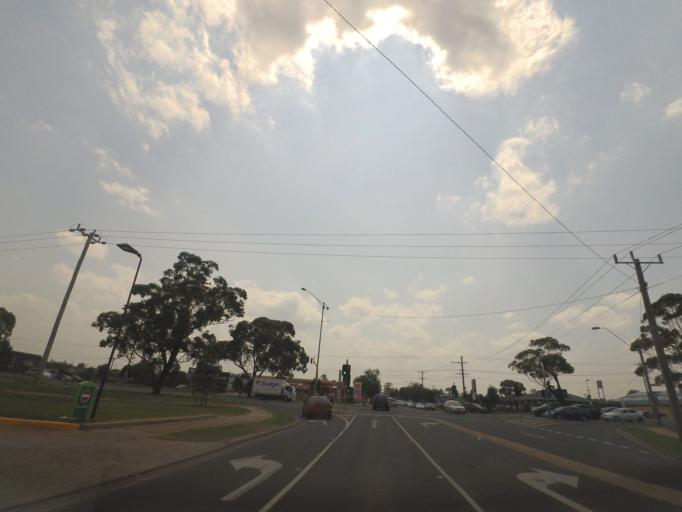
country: AU
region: Victoria
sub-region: Melton
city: Melton
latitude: -37.6841
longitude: 144.5780
